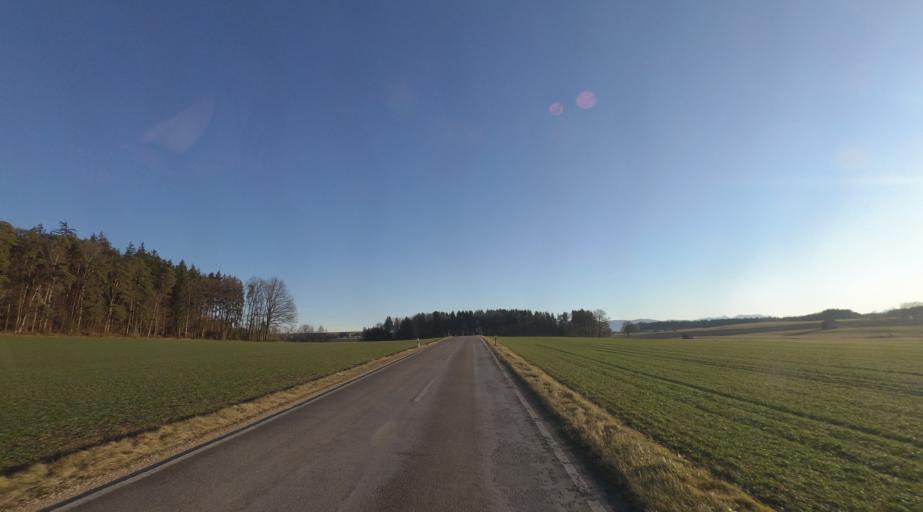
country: DE
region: Bavaria
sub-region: Upper Bavaria
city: Taching am See
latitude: 47.9891
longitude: 12.7673
